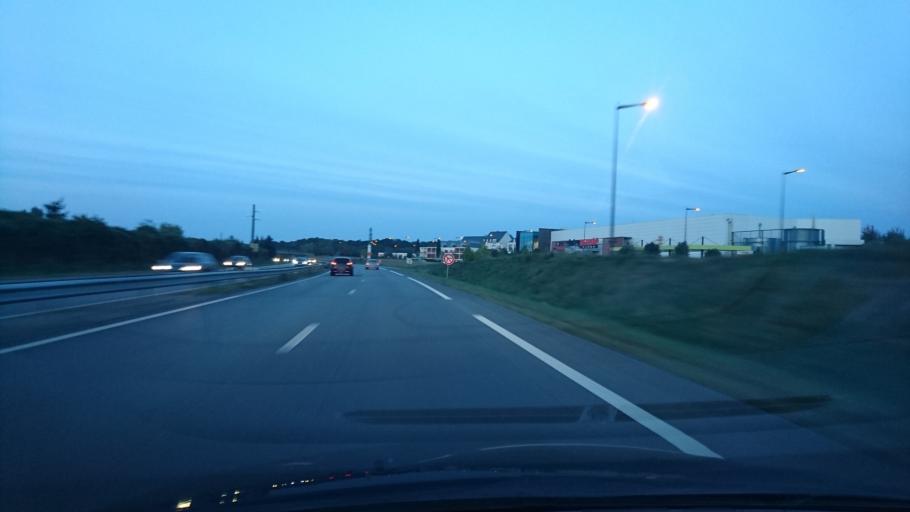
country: FR
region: Brittany
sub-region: Departement d'Ille-et-Vilaine
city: Bruz
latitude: 48.0283
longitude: -1.7639
